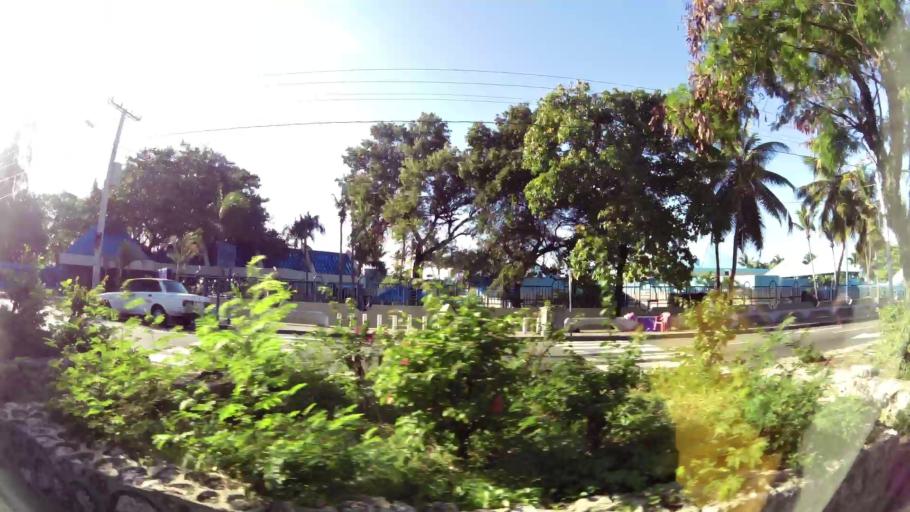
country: DO
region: Santo Domingo
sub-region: Santo Domingo
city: Santo Domingo Este
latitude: 18.4689
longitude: -69.8506
